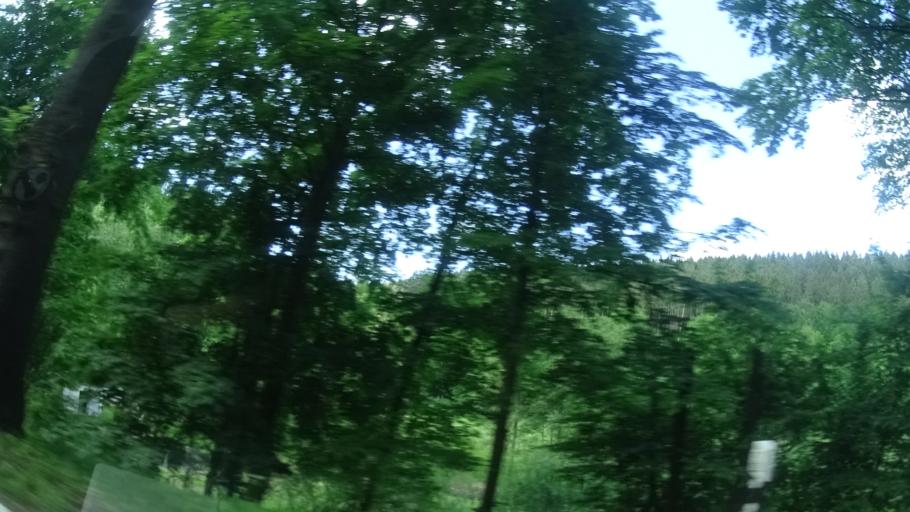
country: DE
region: Thuringia
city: Rosa
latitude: 50.7191
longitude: 10.2739
